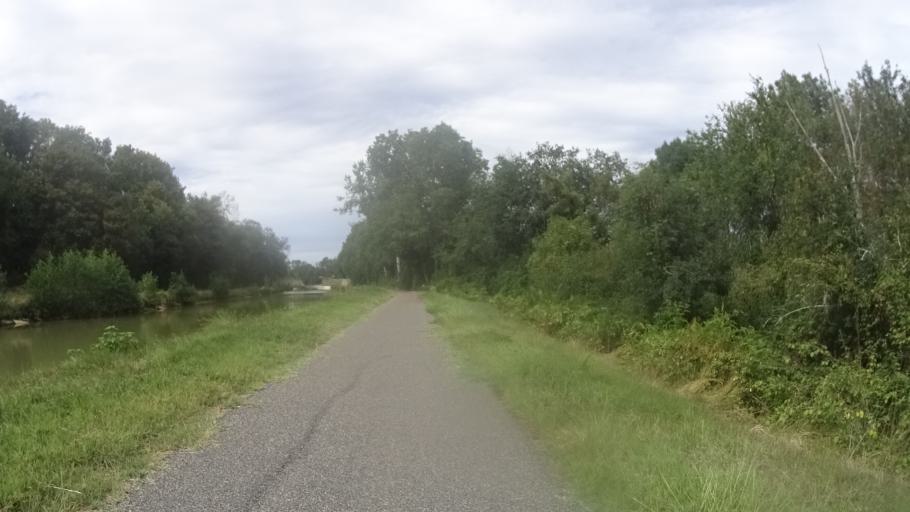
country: FR
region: Bourgogne
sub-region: Departement de la Nievre
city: Sermoise-sur-Loire
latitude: 46.9569
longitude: 3.1990
